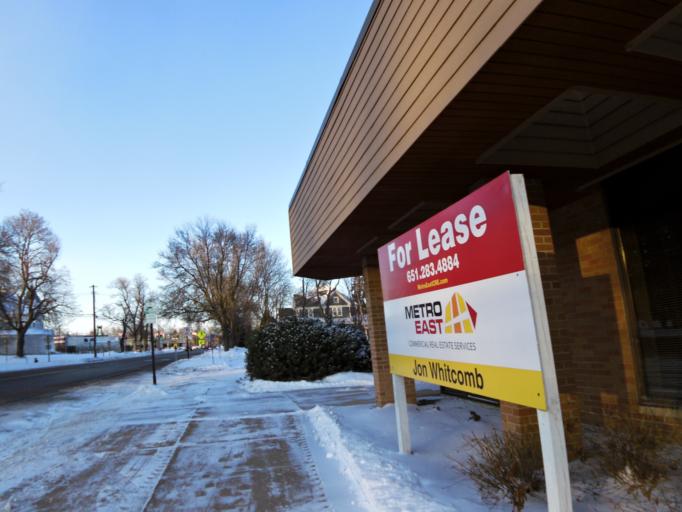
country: US
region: Minnesota
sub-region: Washington County
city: Lake Elmo
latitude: 45.0004
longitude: -92.8800
